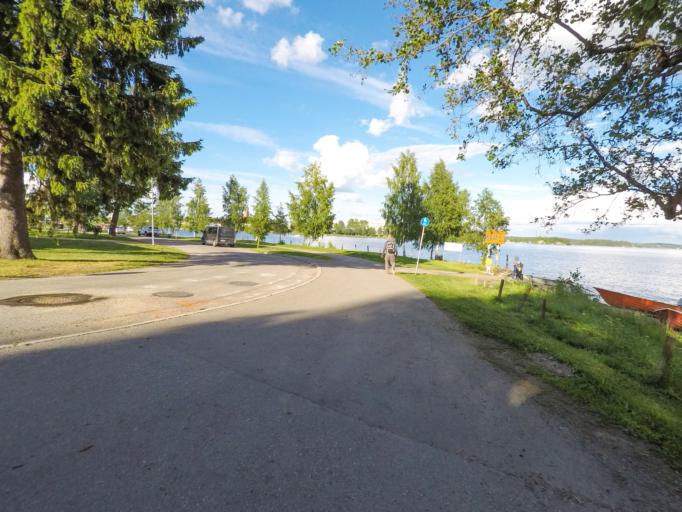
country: FI
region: Southern Savonia
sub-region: Savonlinna
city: Savonlinna
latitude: 61.8638
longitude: 28.8658
